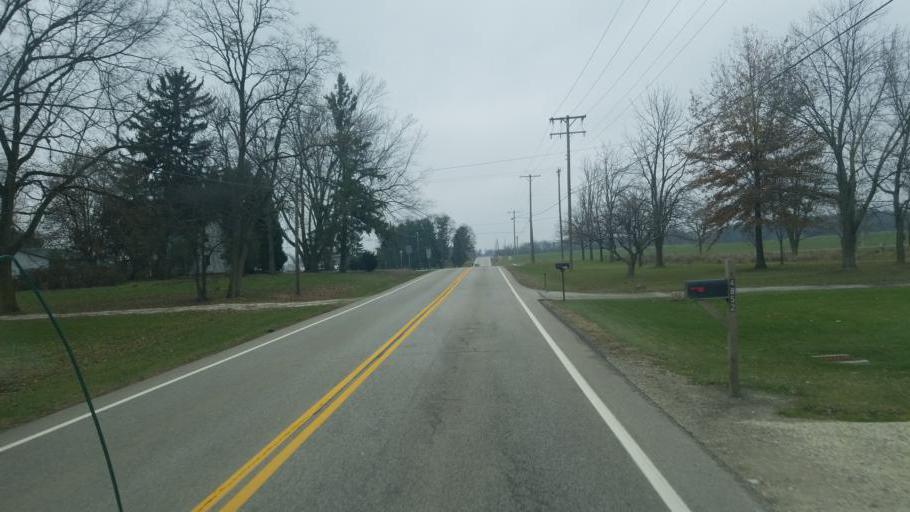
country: US
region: Ohio
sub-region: Medina County
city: Medina
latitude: 41.1412
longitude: -81.9236
